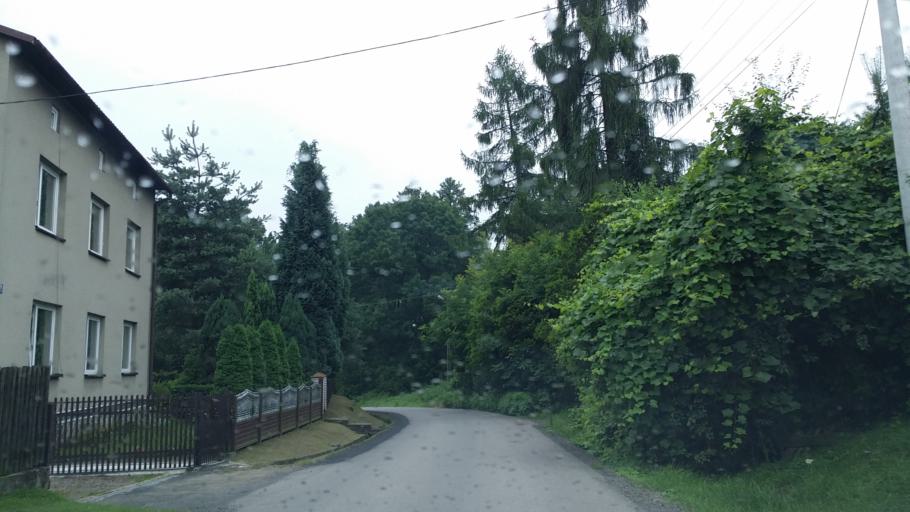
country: PL
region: Lesser Poland Voivodeship
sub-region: Powiat wadowicki
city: Spytkowice
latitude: 49.9878
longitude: 19.5021
